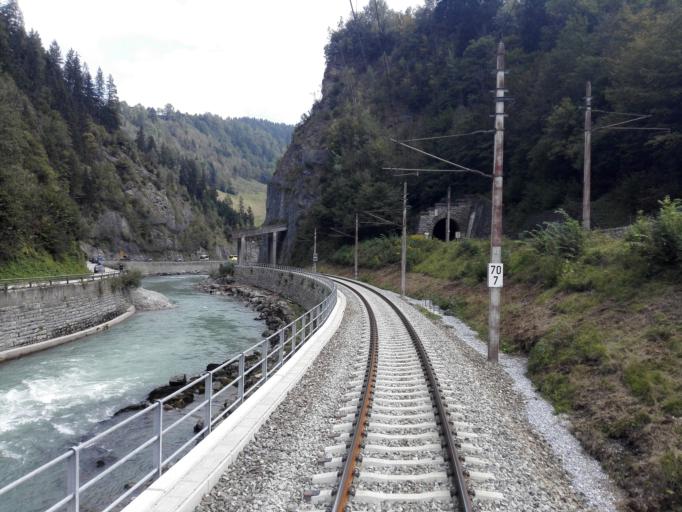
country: AT
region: Salzburg
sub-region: Politischer Bezirk Sankt Johann im Pongau
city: Goldegg
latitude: 47.3041
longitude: 13.1098
